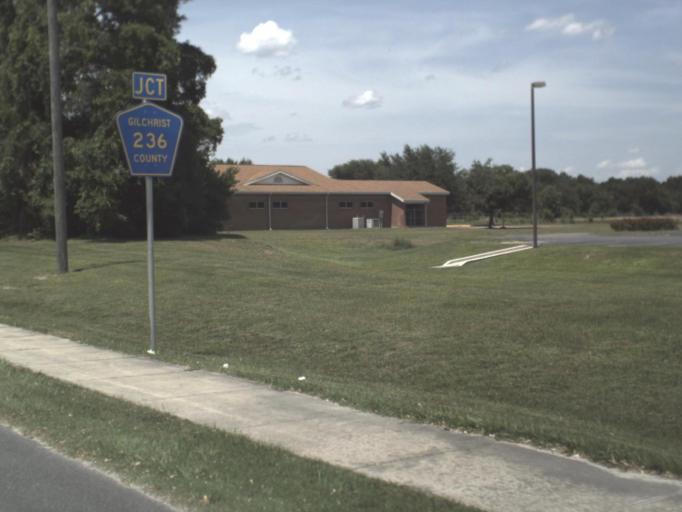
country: US
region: Florida
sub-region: Gilchrist County
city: Trenton
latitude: 29.7647
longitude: -82.8664
